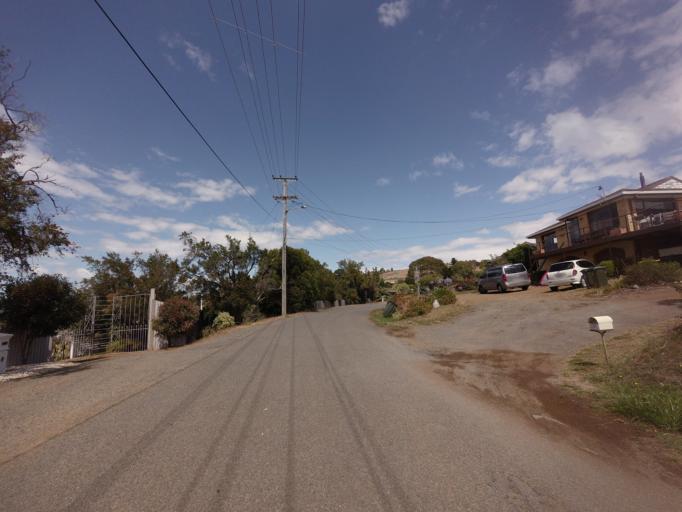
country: AU
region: Tasmania
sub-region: Clarence
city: Rokeby
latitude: -42.9101
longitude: 147.4327
